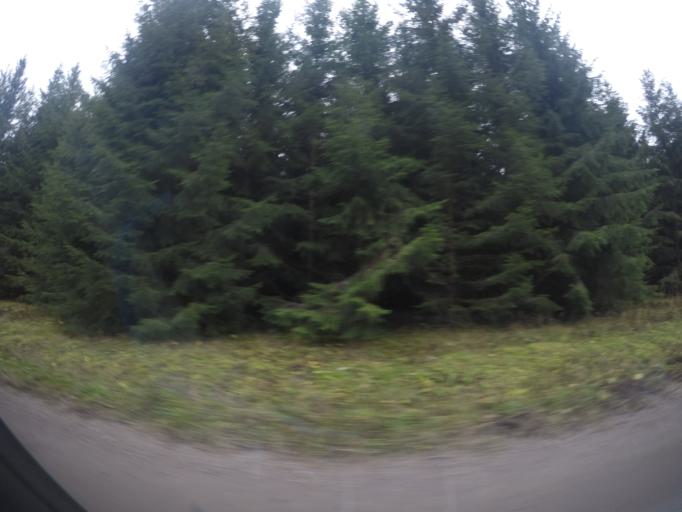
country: SE
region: Vaestmanland
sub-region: Surahammars Kommun
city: Ramnas
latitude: 59.7330
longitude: 16.1113
